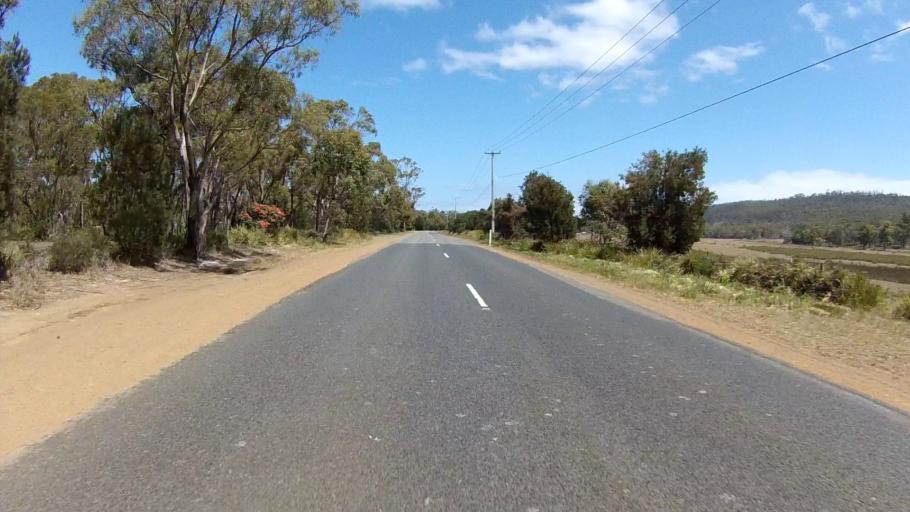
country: AU
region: Tasmania
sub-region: Clarence
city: Sandford
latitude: -42.9390
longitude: 147.4894
